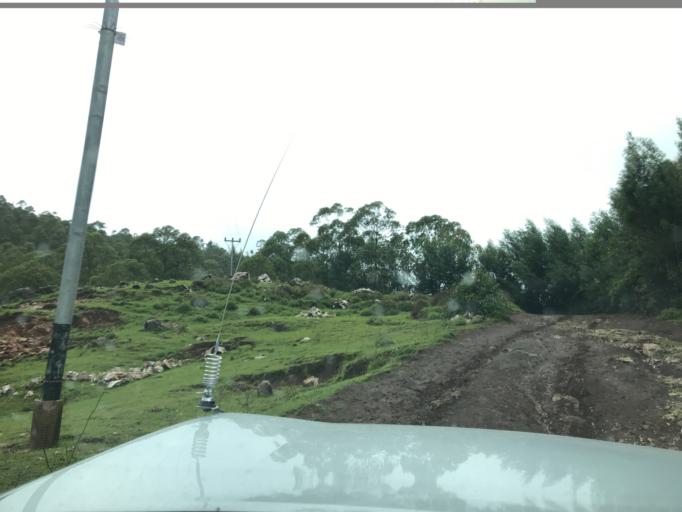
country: TL
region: Ainaro
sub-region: Ainaro
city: Ainaro
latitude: -8.8765
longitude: 125.5529
